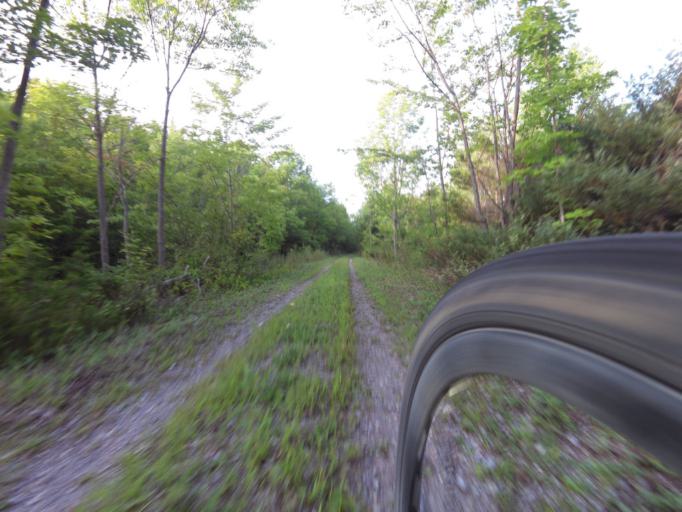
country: CA
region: Ontario
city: Gananoque
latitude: 44.5379
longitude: -76.4037
